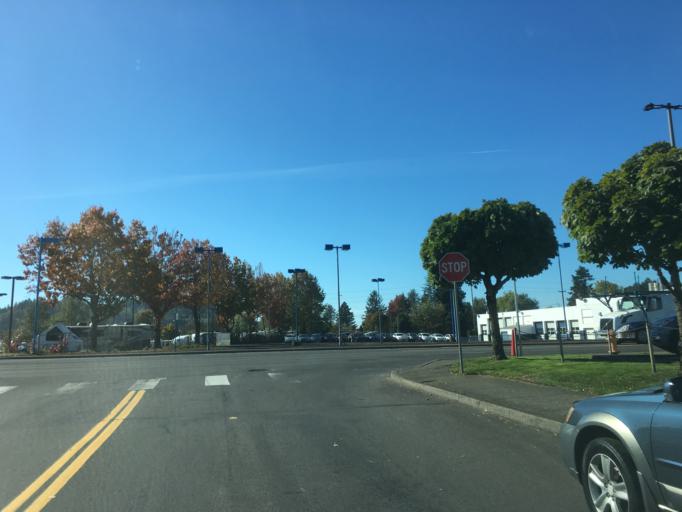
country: US
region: Oregon
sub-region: Multnomah County
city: Gresham
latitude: 45.4959
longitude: -122.4115
